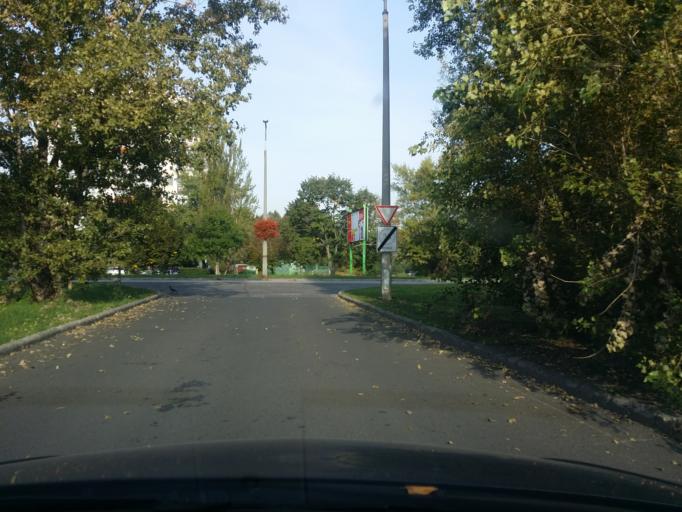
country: HU
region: Budapest
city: Budapest XV. keruelet
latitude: 47.5787
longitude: 19.1080
